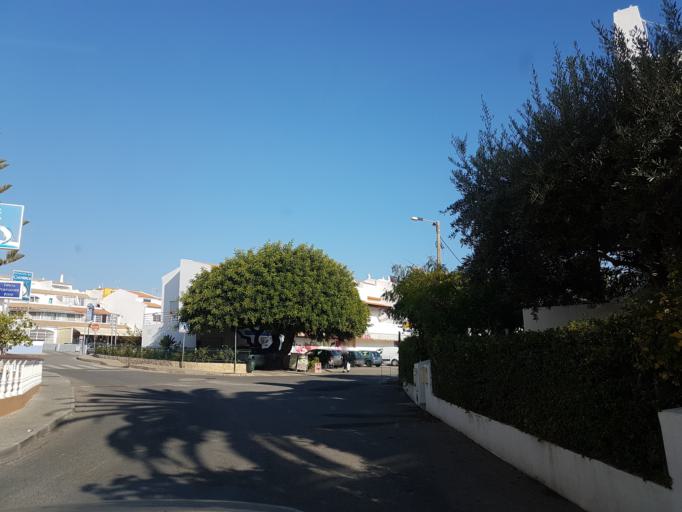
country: PT
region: Faro
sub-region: Loule
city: Boliqueime
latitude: 37.0928
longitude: -8.1910
